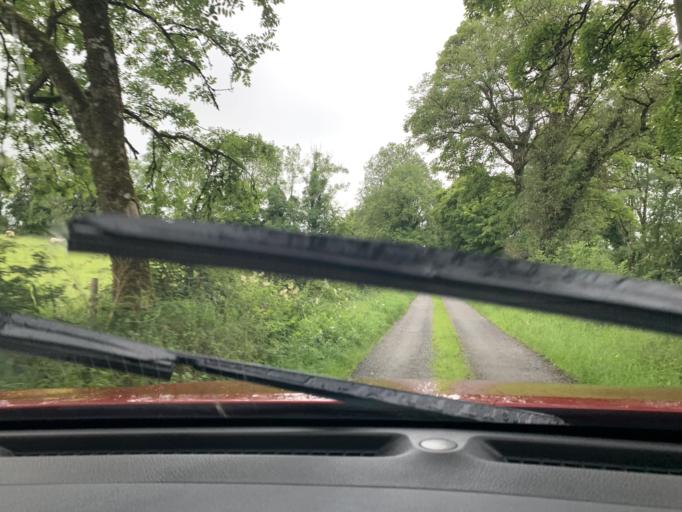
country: IE
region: Connaught
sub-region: County Leitrim
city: Carrick-on-Shannon
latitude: 53.8729
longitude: -8.1348
